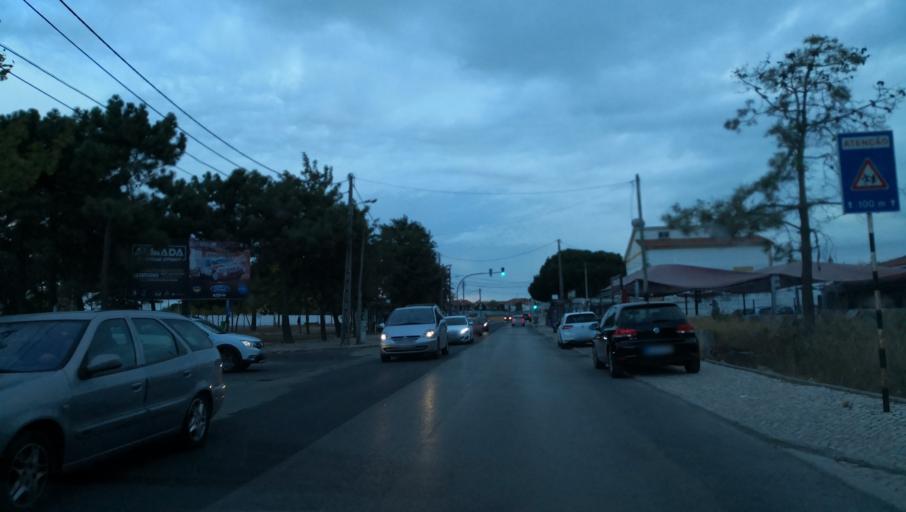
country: PT
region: Setubal
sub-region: Almada
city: Charneca
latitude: 38.6059
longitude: -9.1864
